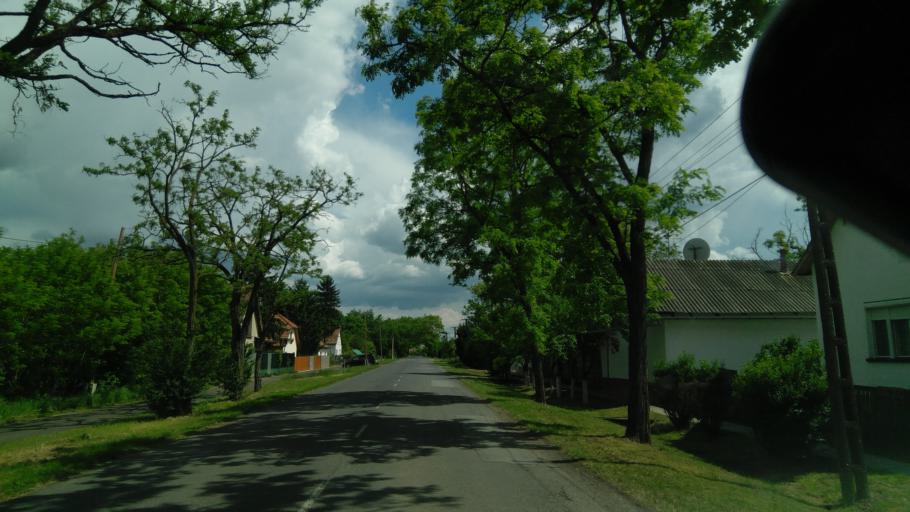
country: HU
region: Bekes
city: Korosladany
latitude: 46.9744
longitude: 21.0598
